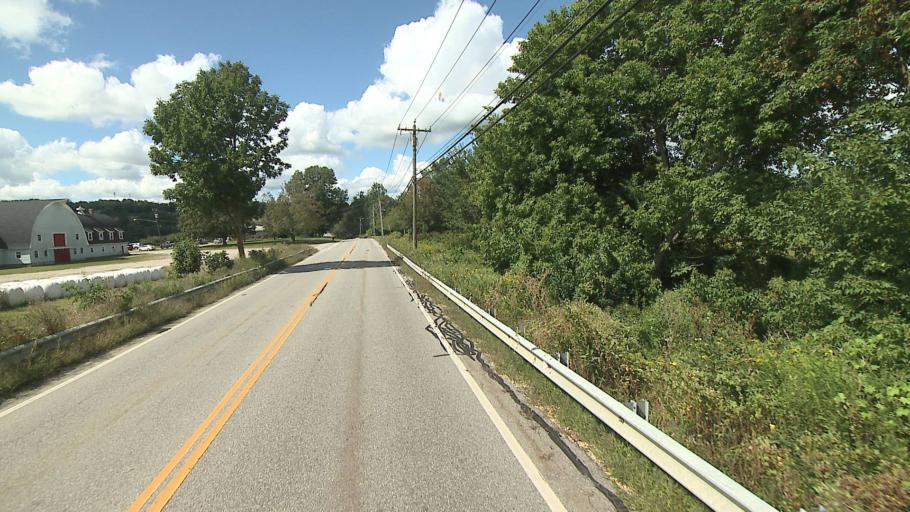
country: US
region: Connecticut
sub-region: Windham County
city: Putnam
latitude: 41.8973
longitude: -71.9383
